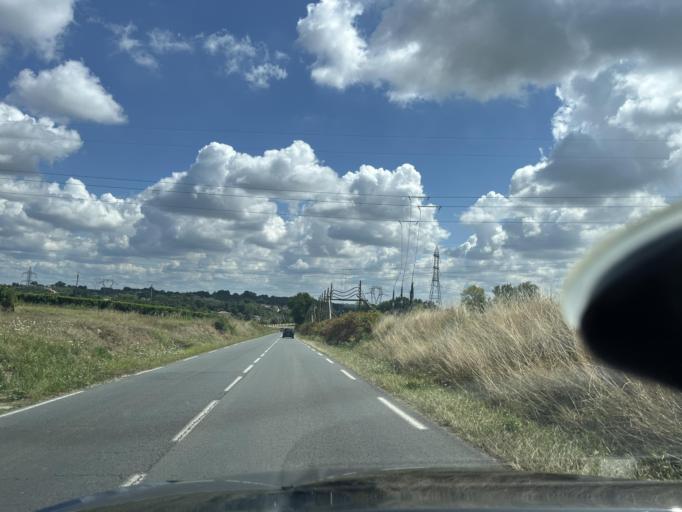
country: FR
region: Aquitaine
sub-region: Departement de la Gironde
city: Bourg
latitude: 45.0387
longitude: -0.5323
